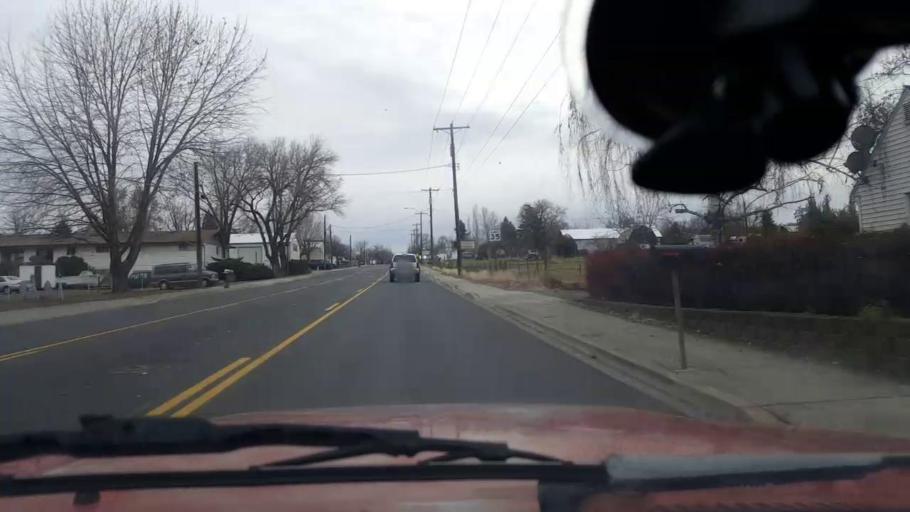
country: US
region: Washington
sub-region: Asotin County
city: West Clarkston-Highland
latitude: 46.4136
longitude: -117.0692
